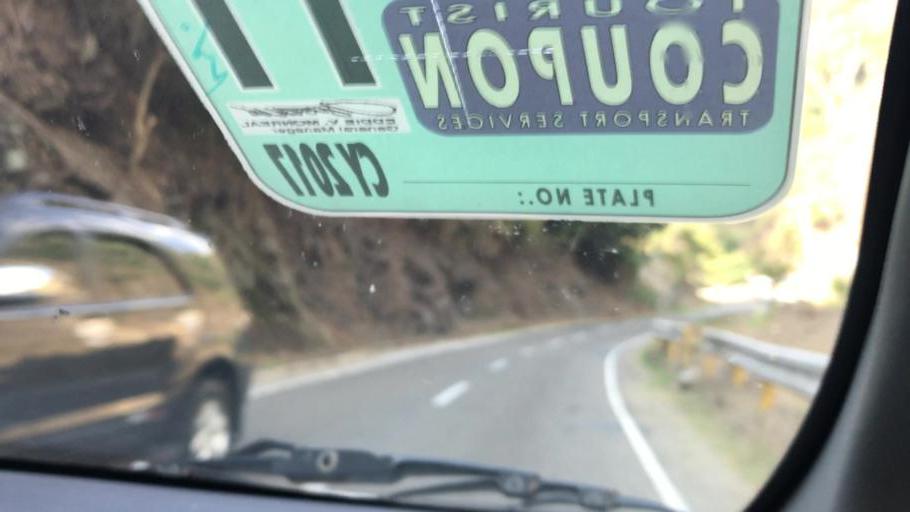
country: PH
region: Cordillera
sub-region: Province of Benguet
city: Tuba
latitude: 16.3215
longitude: 120.6150
